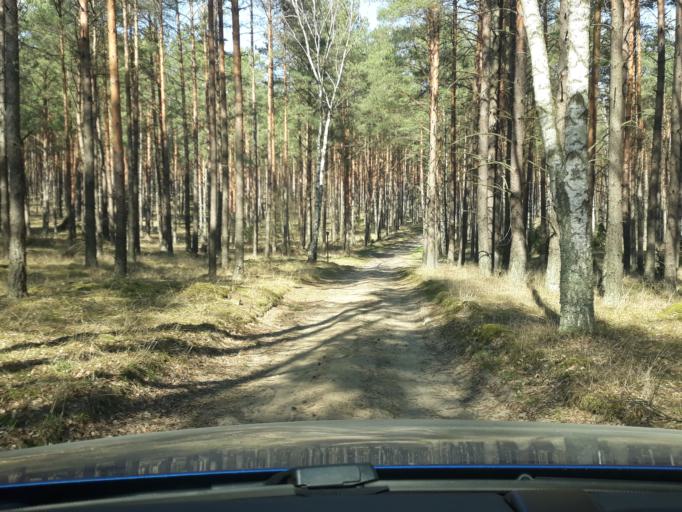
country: PL
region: Pomeranian Voivodeship
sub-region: Powiat bytowski
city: Lipnica
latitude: 53.8643
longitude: 17.4291
